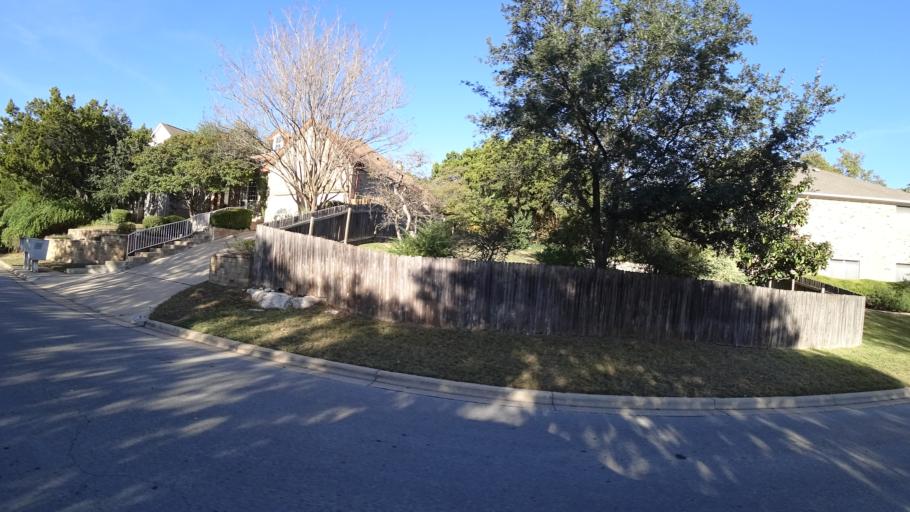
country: US
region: Texas
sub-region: Williamson County
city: Jollyville
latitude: 30.4124
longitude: -97.7710
